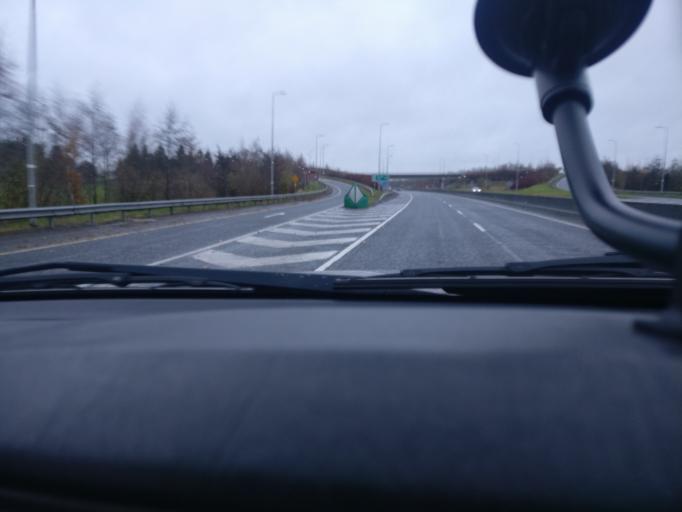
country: IE
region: Leinster
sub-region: An Iarmhi
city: Athlone
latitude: 53.4177
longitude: -7.8901
